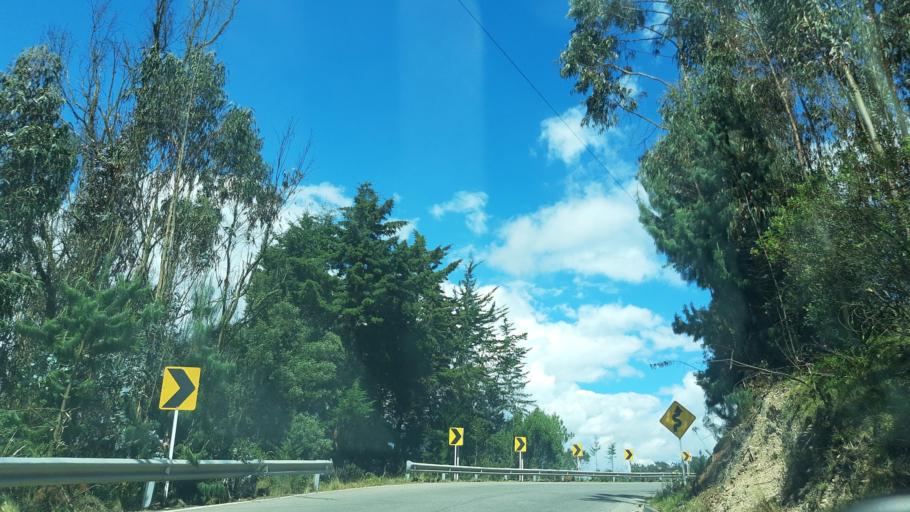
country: CO
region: Boyaca
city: Samaca
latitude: 5.4823
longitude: -73.4747
